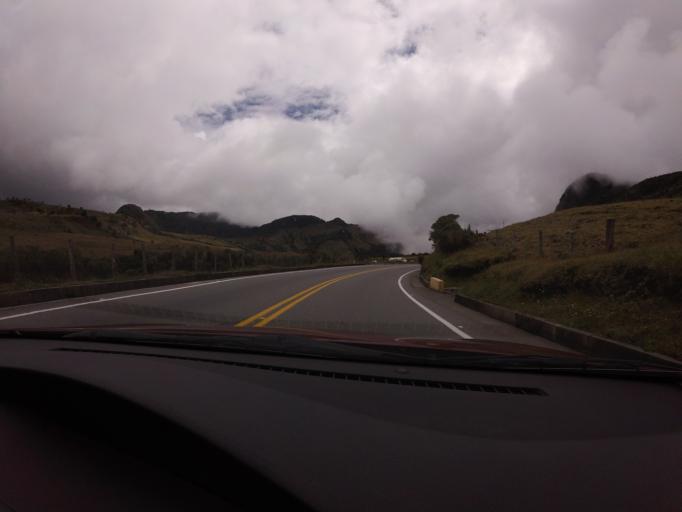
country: CO
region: Tolima
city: Herveo
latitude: 5.0386
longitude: -75.3347
